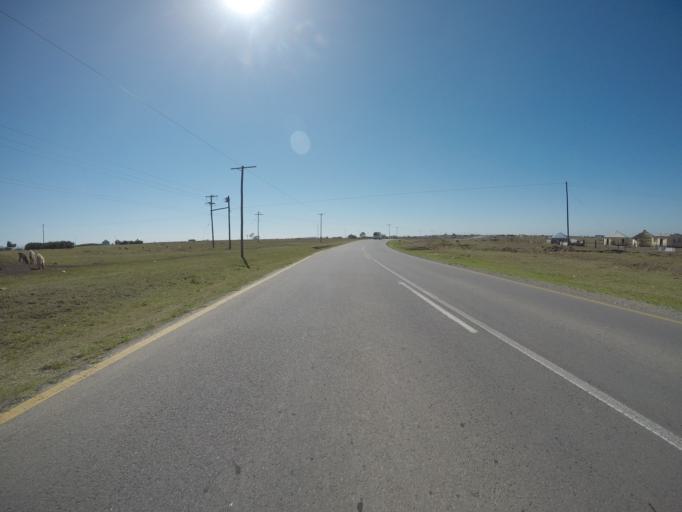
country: ZA
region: Eastern Cape
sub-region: OR Tambo District Municipality
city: Mthatha
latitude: -31.8920
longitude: 28.7772
